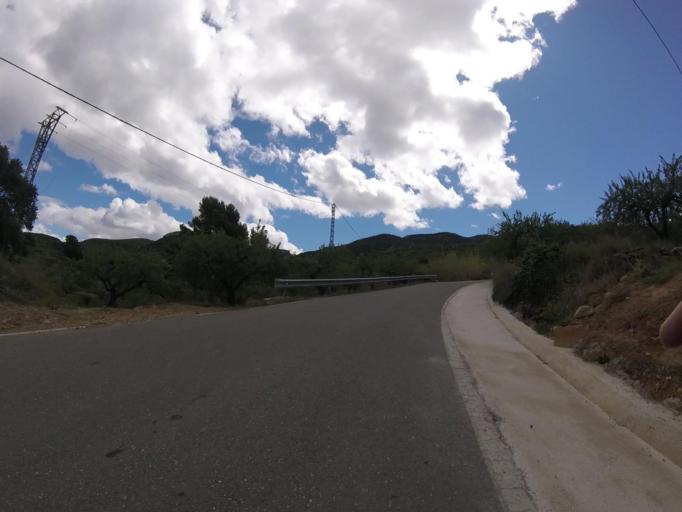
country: ES
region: Valencia
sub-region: Provincia de Castello
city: Sierra-Engarceran
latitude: 40.2957
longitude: -0.0410
